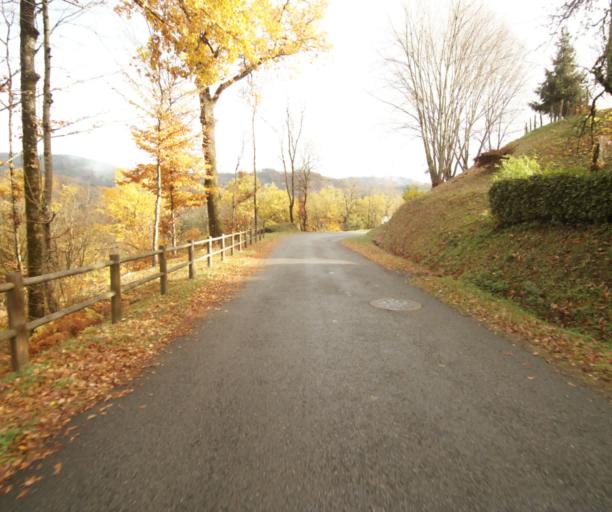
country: FR
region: Limousin
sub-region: Departement de la Correze
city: Cornil
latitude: 45.2146
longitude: 1.6456
